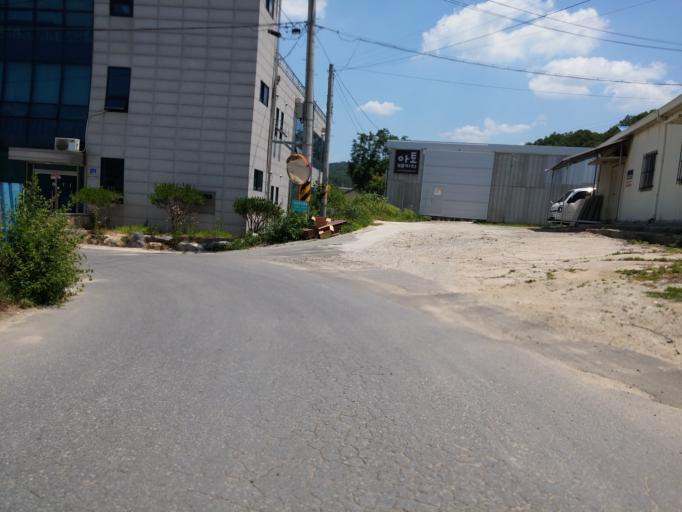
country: KR
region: Chungcheongbuk-do
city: Cheongju-si
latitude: 36.5616
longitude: 127.4405
